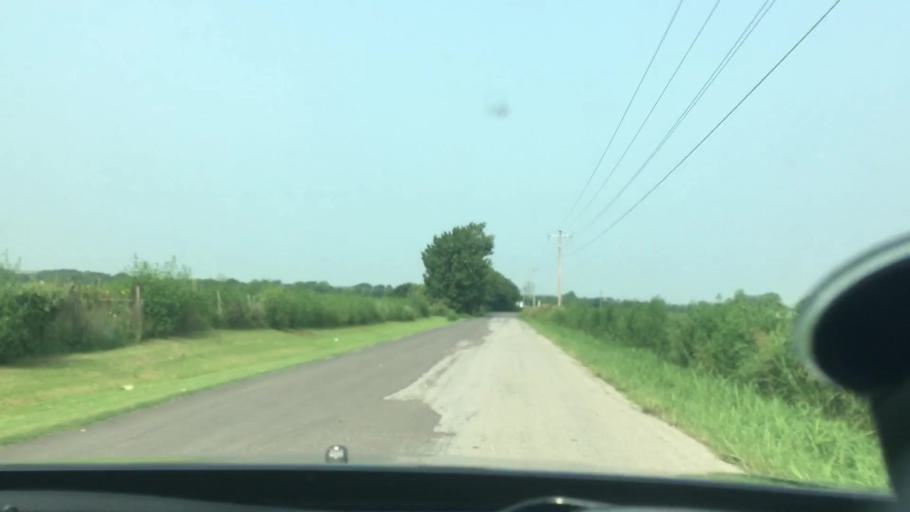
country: US
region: Oklahoma
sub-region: Garvin County
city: Lindsay
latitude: 34.8102
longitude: -97.6118
